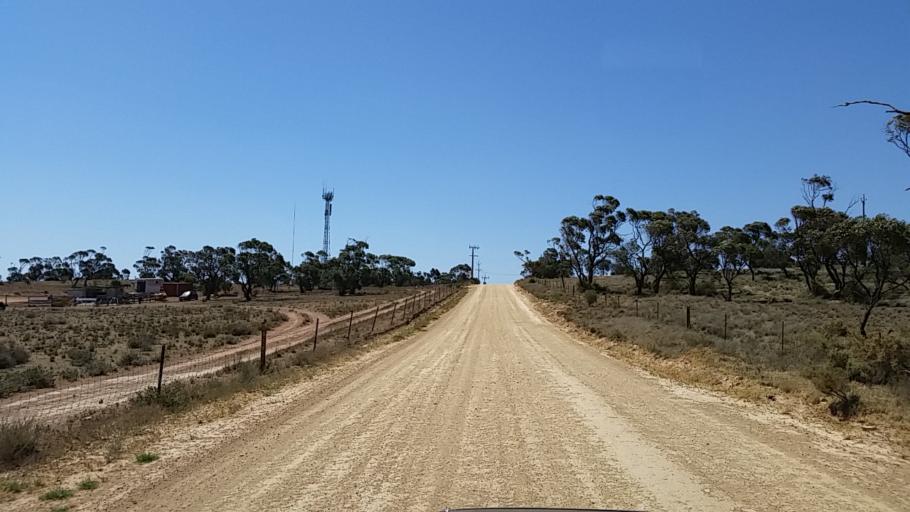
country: AU
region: South Australia
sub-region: Peterborough
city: Peterborough
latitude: -32.9838
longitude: 138.8318
